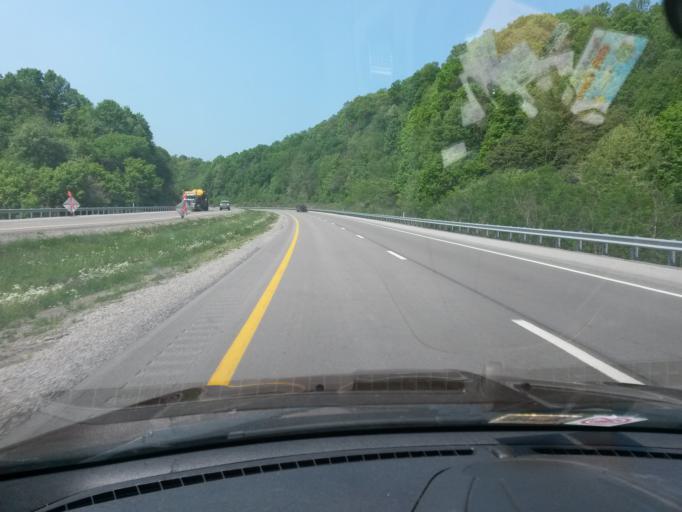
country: US
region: West Virginia
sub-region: Lewis County
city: Weston
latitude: 38.9017
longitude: -80.6180
